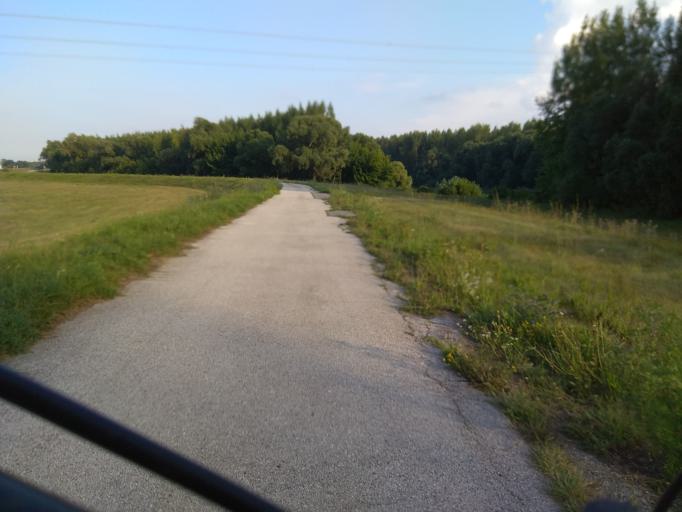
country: SK
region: Trnavsky
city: Gabcikovo
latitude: 47.8005
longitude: 17.6503
